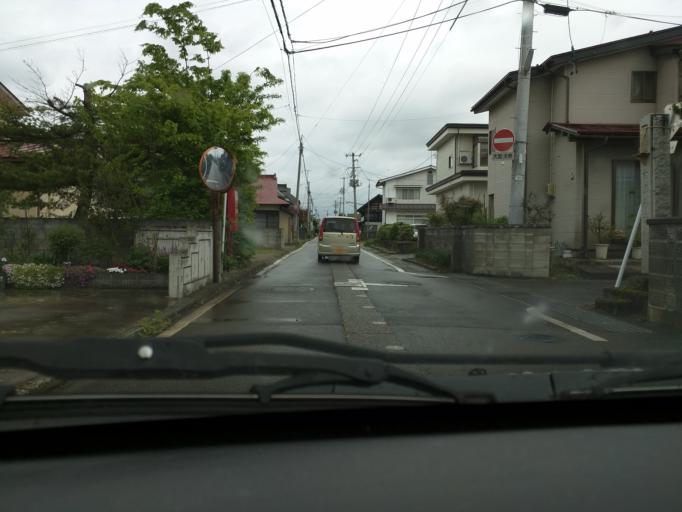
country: JP
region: Fukushima
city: Kitakata
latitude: 37.5875
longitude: 139.8864
